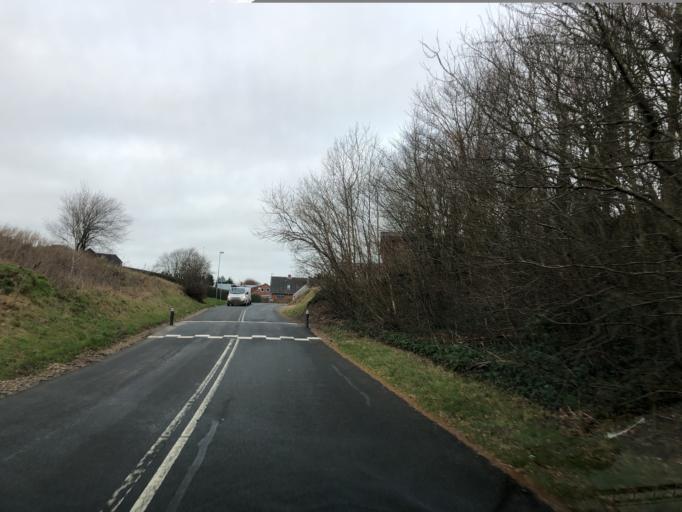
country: DK
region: Central Jutland
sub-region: Viborg Kommune
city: Stoholm
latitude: 56.4461
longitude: 9.1081
